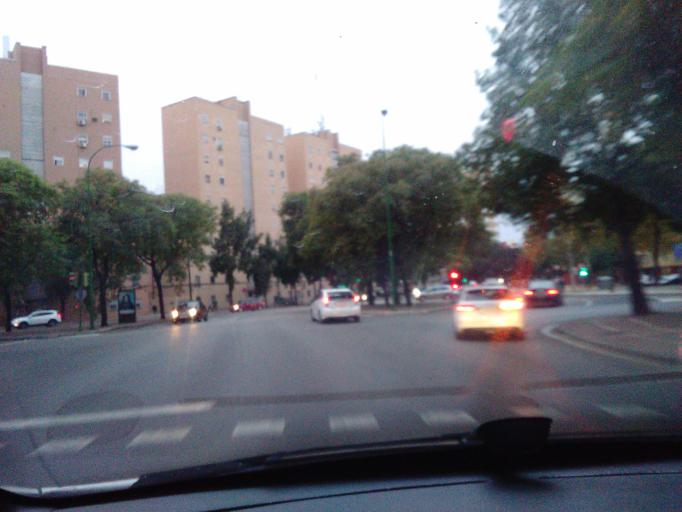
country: ES
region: Andalusia
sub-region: Provincia de Sevilla
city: Sevilla
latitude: 37.3732
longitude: -5.9732
